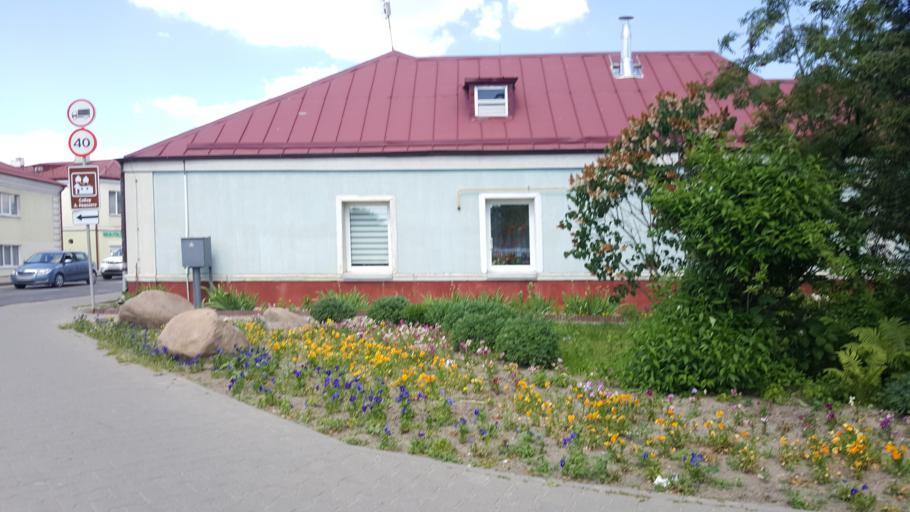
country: BY
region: Brest
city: Kobryn
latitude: 52.2132
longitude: 24.3575
